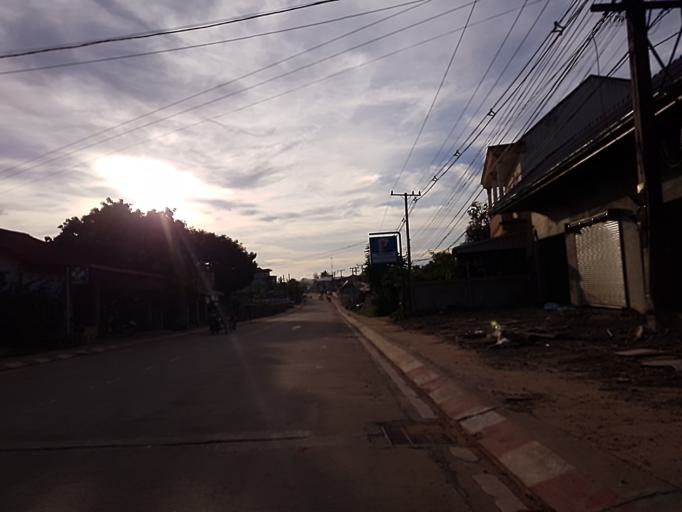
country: TH
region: Nong Khai
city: Si Chiang Mai
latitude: 18.0203
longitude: 102.5056
